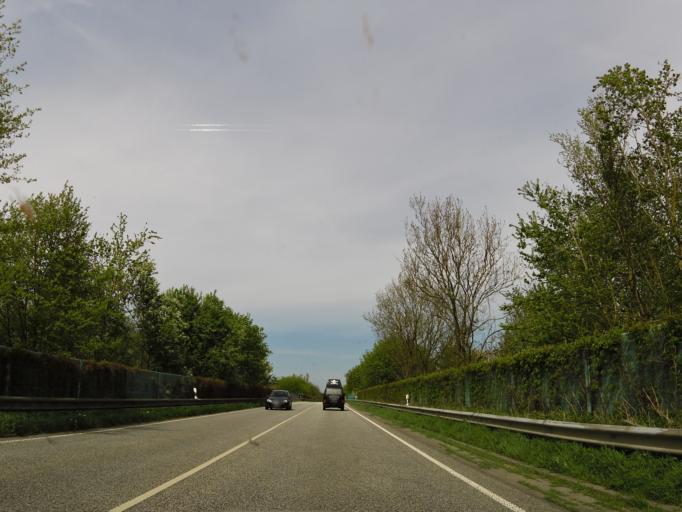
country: DE
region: Schleswig-Holstein
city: Groven
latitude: 54.2901
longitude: 8.9832
